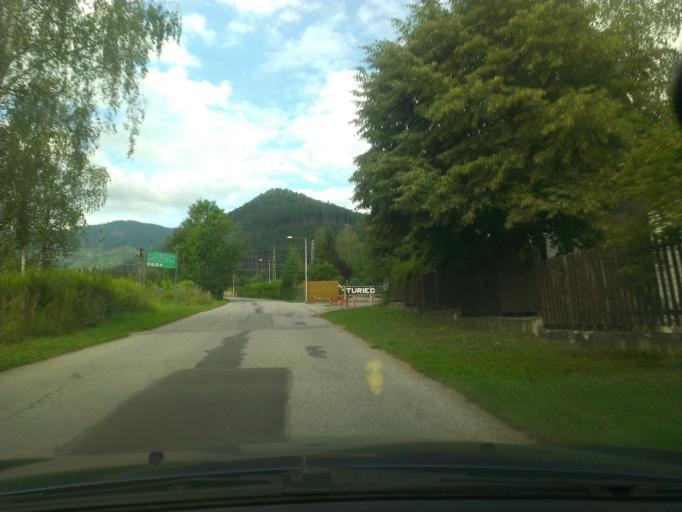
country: SK
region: Zilinsky
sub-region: Okres Zilina
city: Vrutky
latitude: 49.1078
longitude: 18.8997
